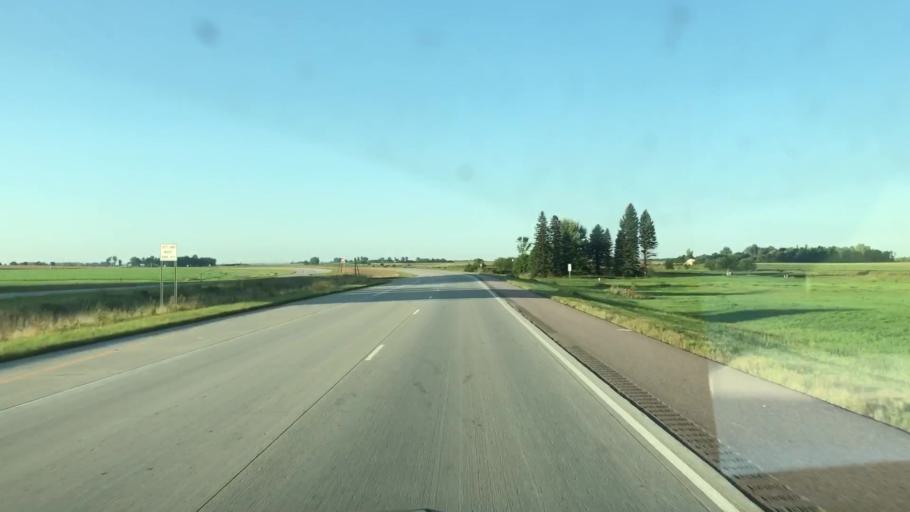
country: US
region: Minnesota
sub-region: Nobles County
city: Worthington
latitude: 43.5789
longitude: -95.6517
